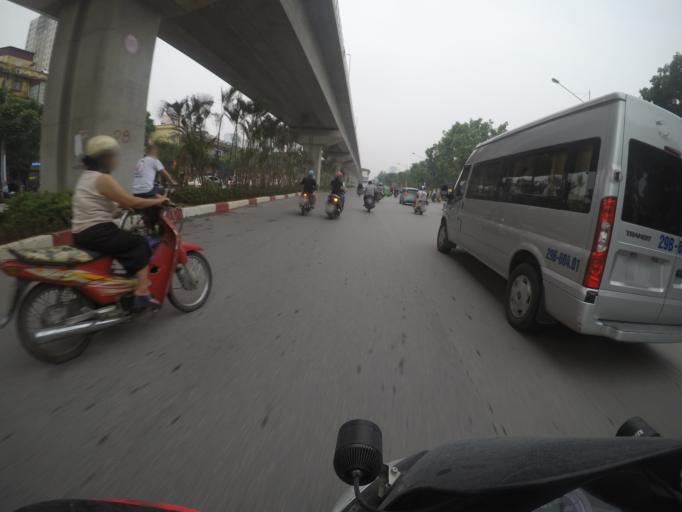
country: VN
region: Ha Noi
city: Thanh Xuan
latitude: 20.9957
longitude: 105.8094
